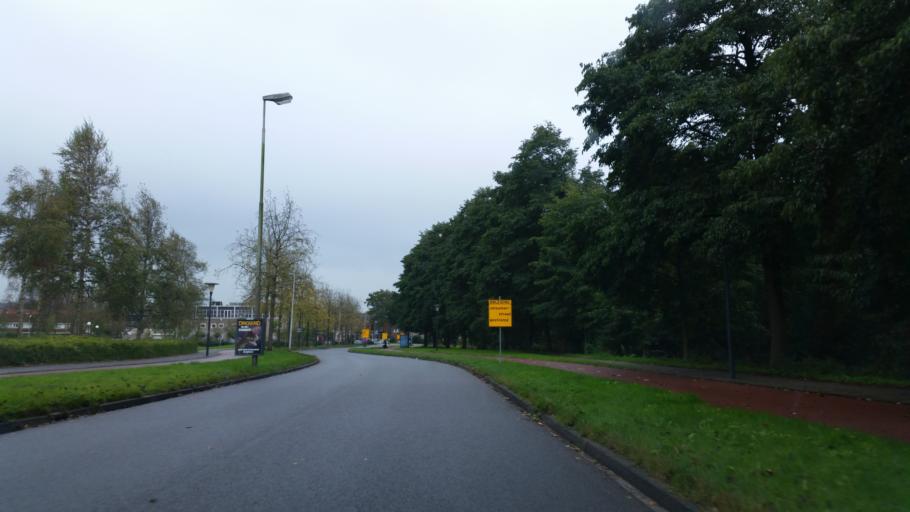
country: NL
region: Friesland
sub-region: Gemeente Leeuwarden
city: Bilgaard
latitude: 53.2091
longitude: 5.7950
